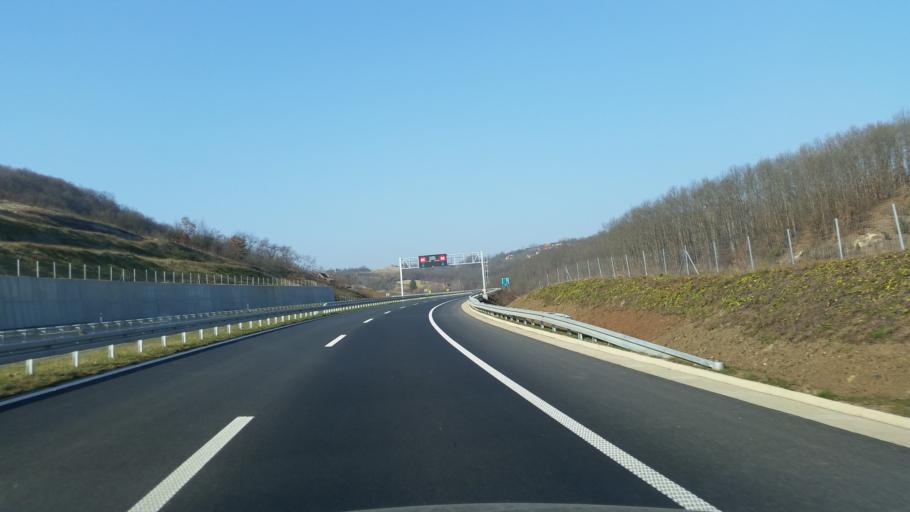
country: RS
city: Prislonica
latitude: 44.0082
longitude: 20.3873
